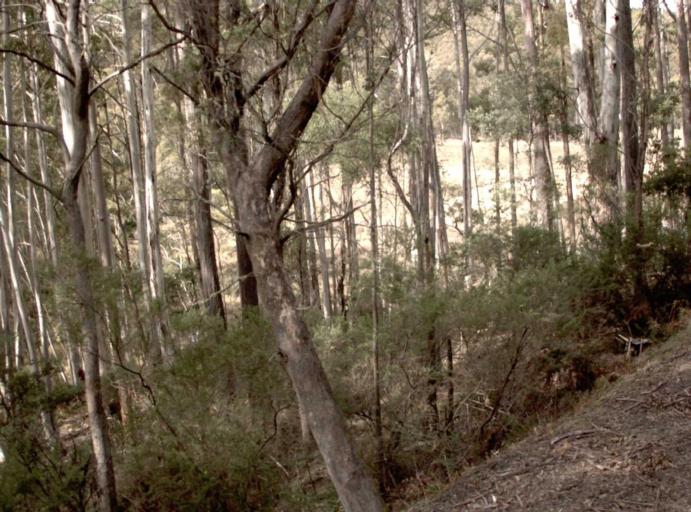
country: AU
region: Tasmania
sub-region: Northern Midlands
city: Evandale
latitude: -41.4574
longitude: 147.4725
